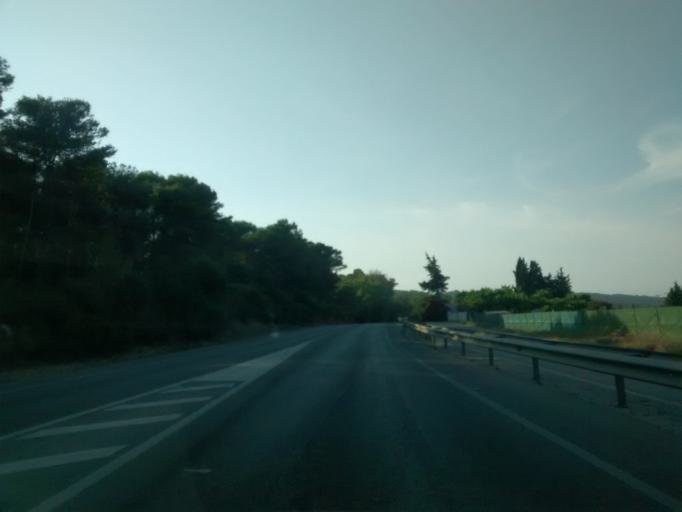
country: ES
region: Andalusia
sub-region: Provincia de Cadiz
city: Barbate de Franco
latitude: 36.2175
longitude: -5.9449
